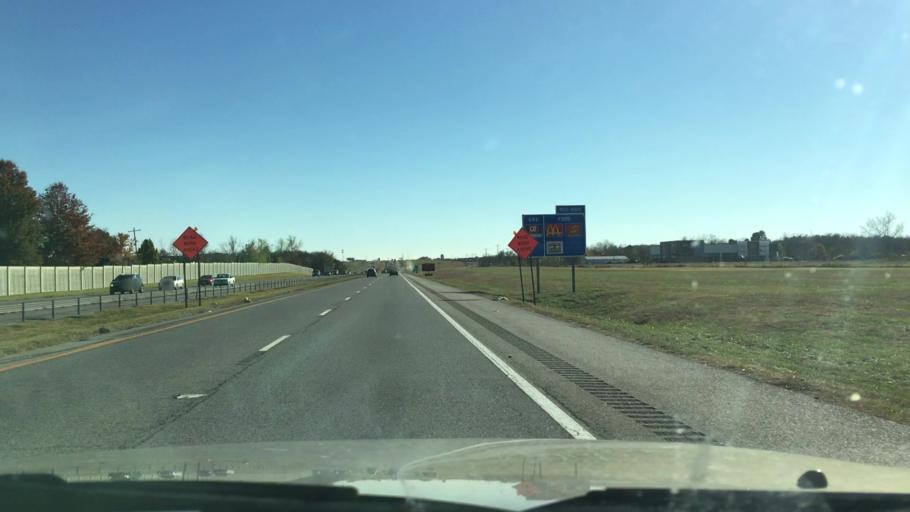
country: US
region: Oklahoma
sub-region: Tulsa County
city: Glenpool
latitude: 35.9992
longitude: -96.0118
